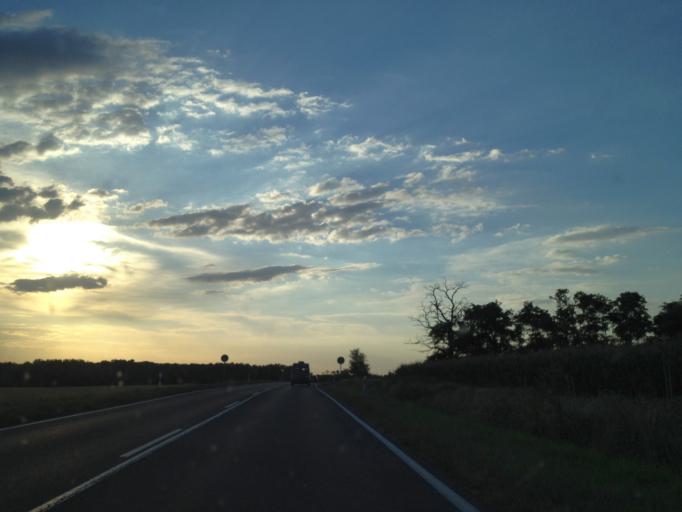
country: HU
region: Gyor-Moson-Sopron
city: Mosonszentmiklos
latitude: 47.7493
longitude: 17.4547
